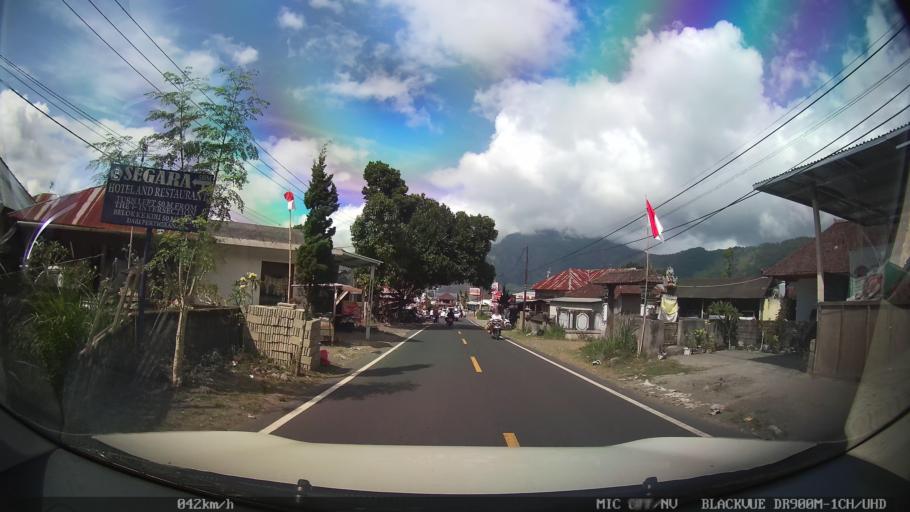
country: ID
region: Bali
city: Banjar Kedisan
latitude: -8.2791
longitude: 115.3778
